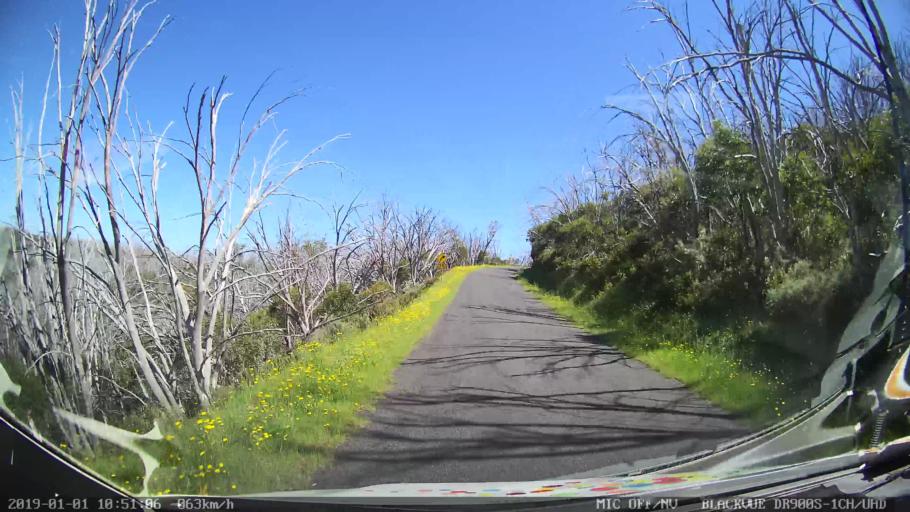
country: AU
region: New South Wales
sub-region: Snowy River
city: Jindabyne
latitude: -36.0223
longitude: 148.3714
